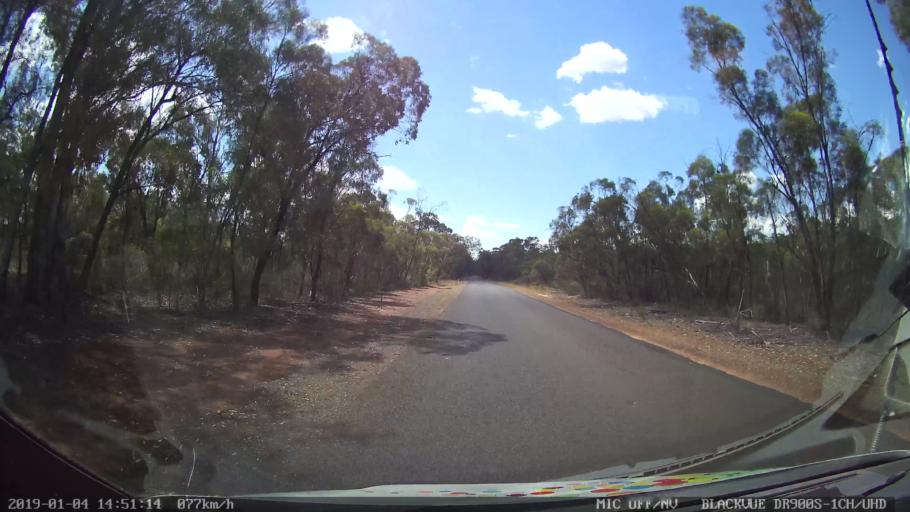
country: AU
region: New South Wales
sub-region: Dubbo Municipality
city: Dubbo
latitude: -32.0293
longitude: 148.6533
